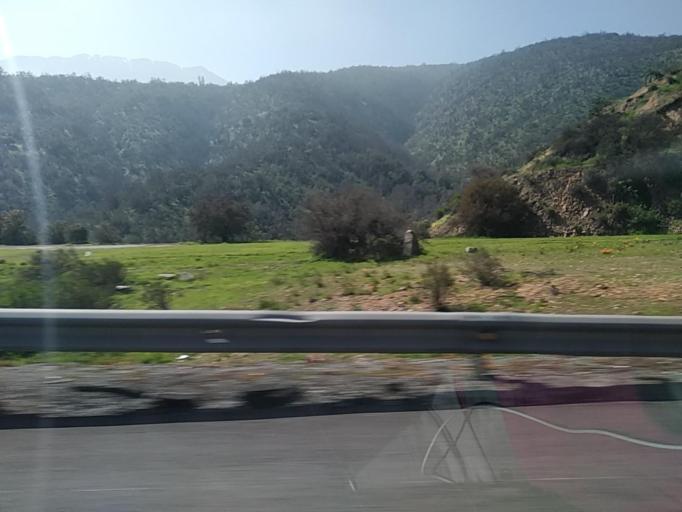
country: CL
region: Santiago Metropolitan
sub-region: Provincia de Talagante
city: Penaflor
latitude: -33.4514
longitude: -70.9778
